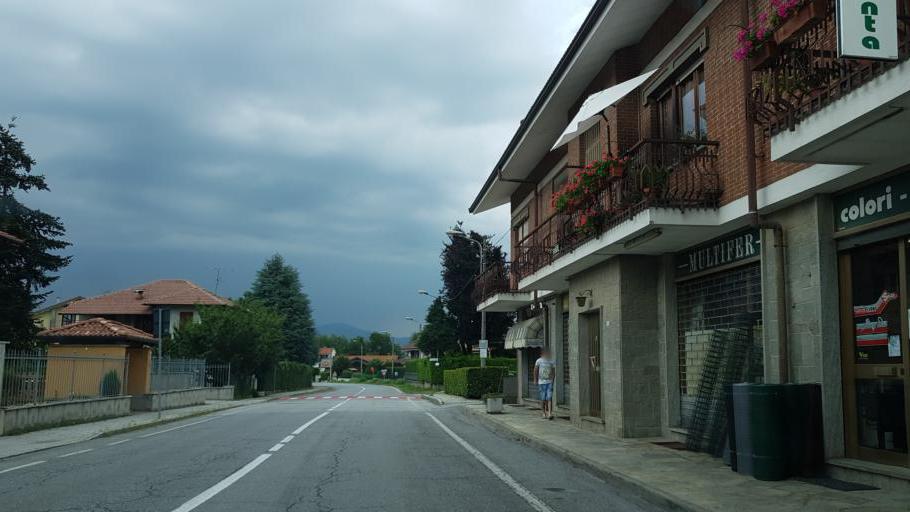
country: IT
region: Piedmont
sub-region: Provincia di Cuneo
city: Cervasca
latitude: 44.3833
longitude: 7.4676
